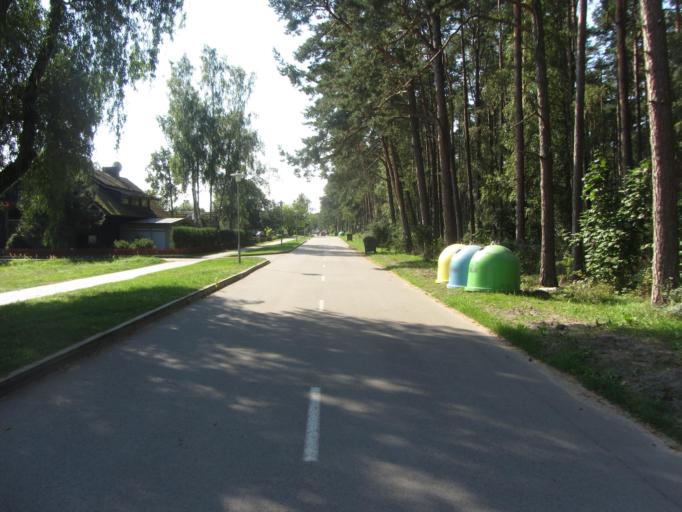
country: LT
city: Neringa
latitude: 55.3710
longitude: 21.0615
